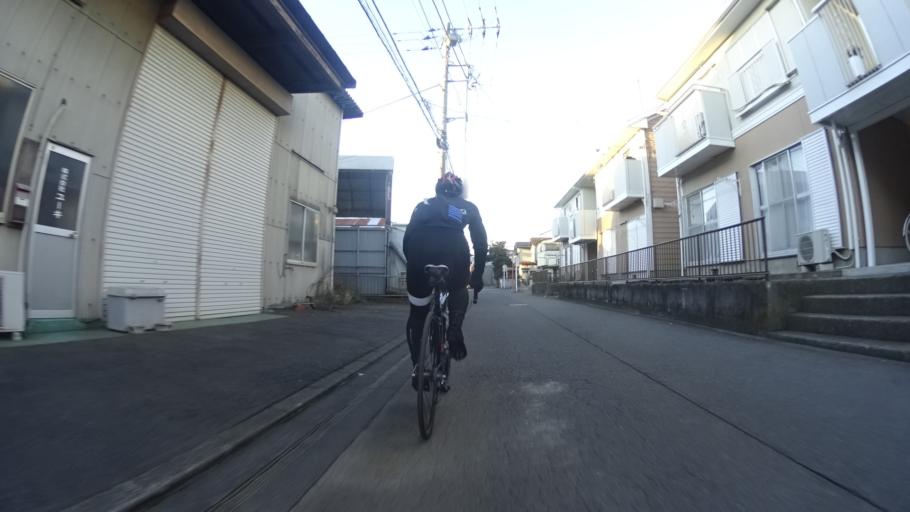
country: JP
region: Kanagawa
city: Atsugi
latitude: 35.4659
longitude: 139.3707
